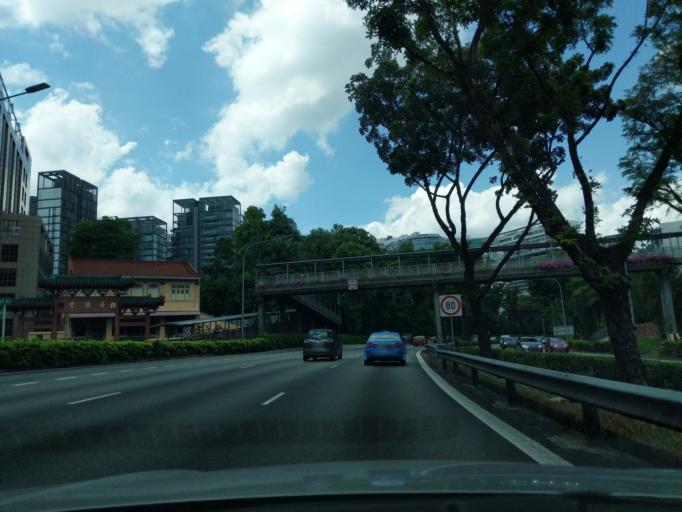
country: SG
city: Singapore
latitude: 1.3029
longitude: 103.8406
